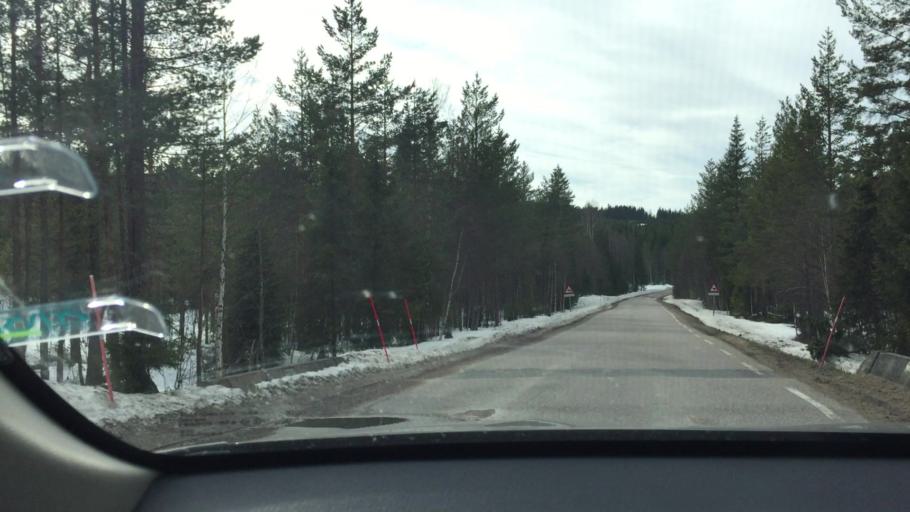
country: NO
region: Hedmark
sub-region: Trysil
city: Innbygda
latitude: 61.0672
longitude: 12.5513
